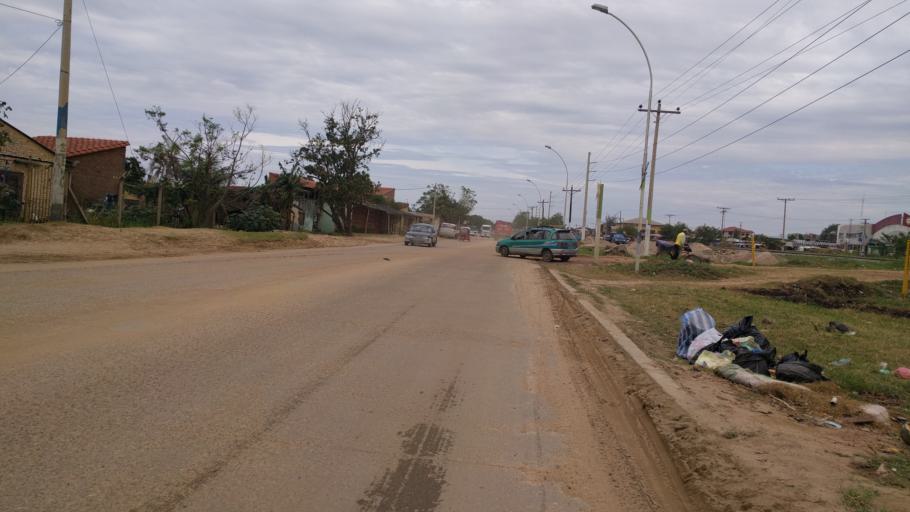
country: BO
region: Santa Cruz
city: Santa Cruz de la Sierra
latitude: -17.8506
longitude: -63.1796
